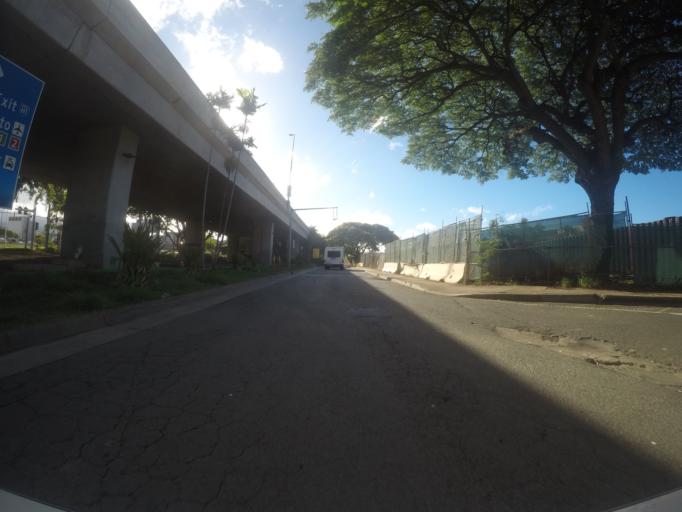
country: US
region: Hawaii
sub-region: Honolulu County
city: Hickam Field
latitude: 21.3344
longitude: -157.9213
